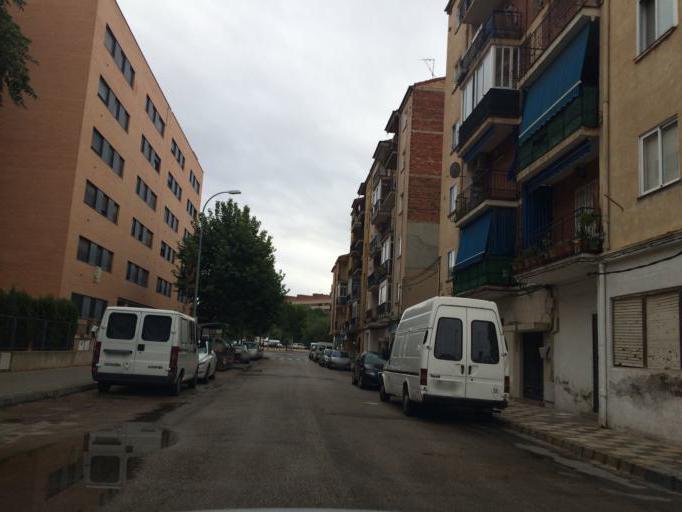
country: ES
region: Castille-La Mancha
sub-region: Provincia de Albacete
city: Albacete
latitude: 39.0039
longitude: -1.8560
